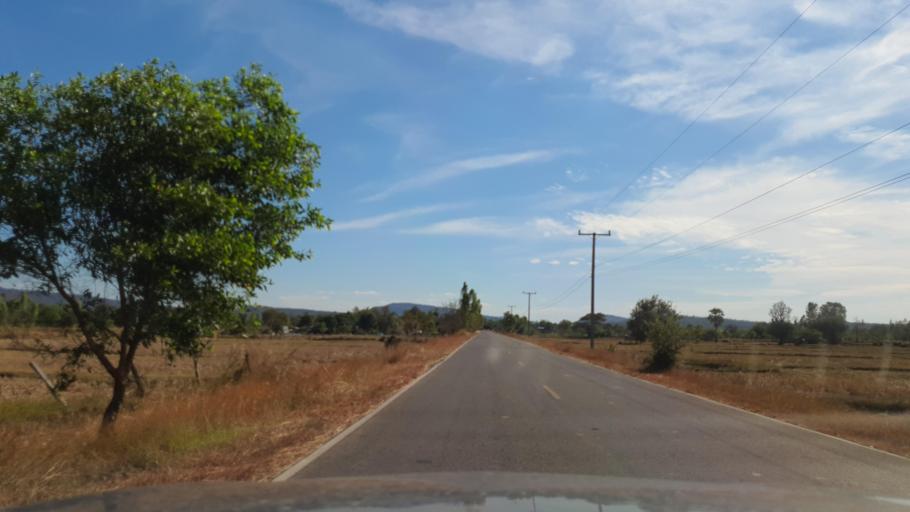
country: TH
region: Kalasin
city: Khao Wong
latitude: 16.6300
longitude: 104.1349
